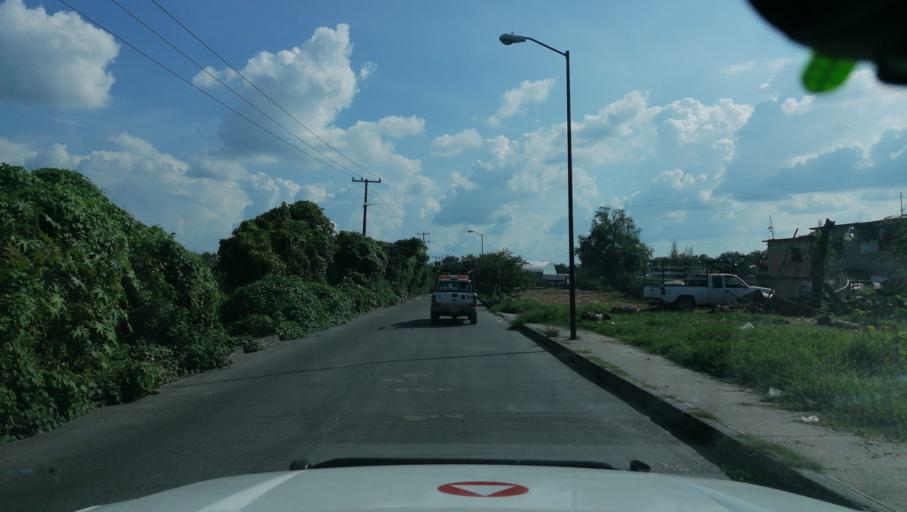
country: MX
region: Morelos
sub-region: Ayala
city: San Pedro Apatlaco
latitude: 18.8052
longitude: -98.9641
